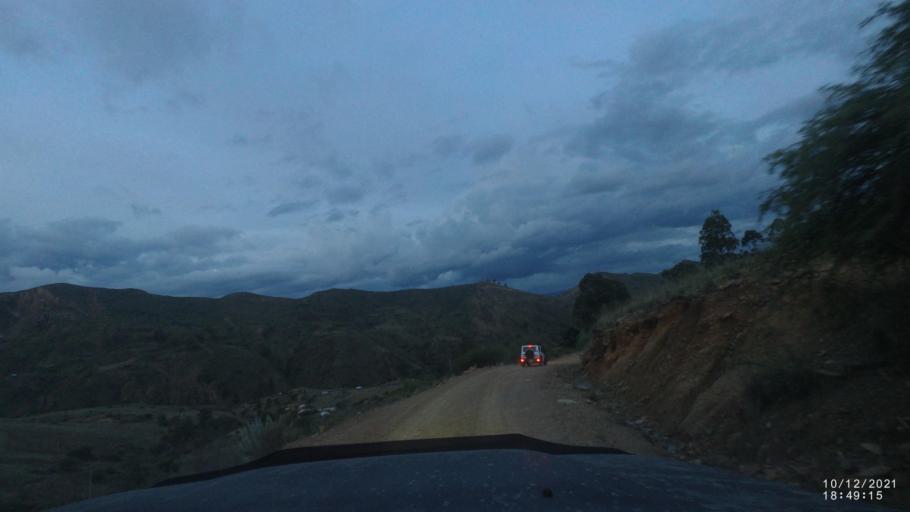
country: BO
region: Cochabamba
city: Tarata
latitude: -17.8815
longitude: -65.9719
